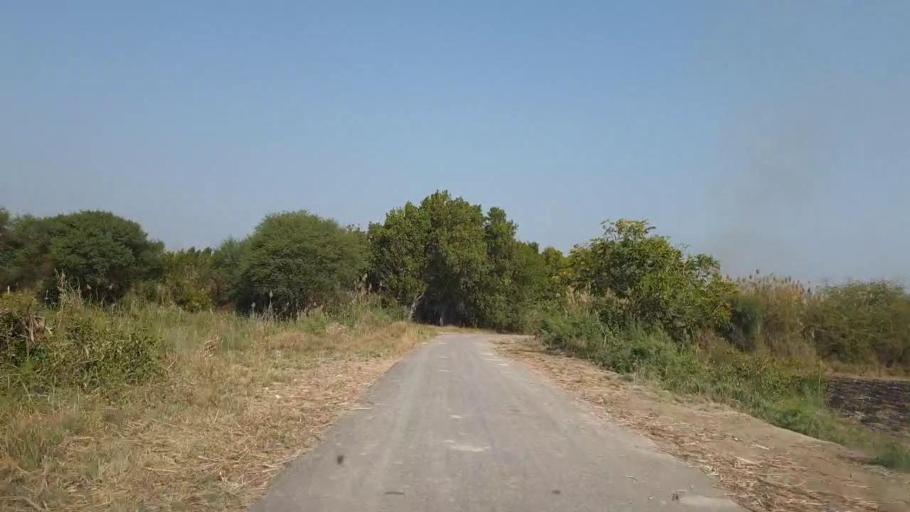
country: PK
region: Sindh
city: Mirpur Khas
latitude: 25.5917
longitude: 69.0021
